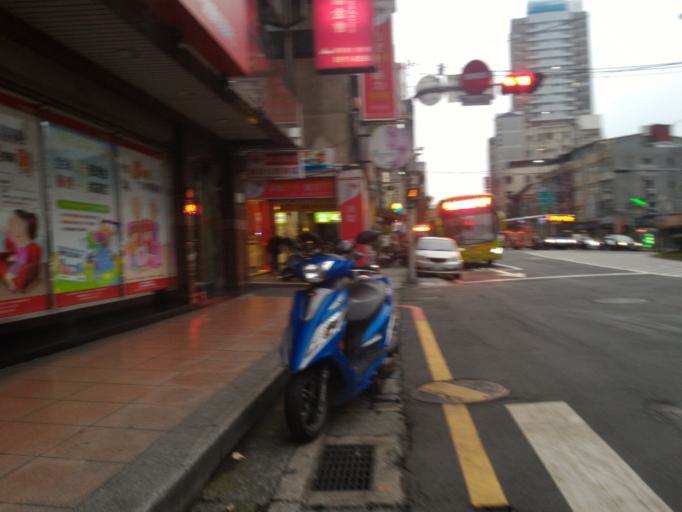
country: TW
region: Taipei
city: Taipei
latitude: 24.9848
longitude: 121.5406
